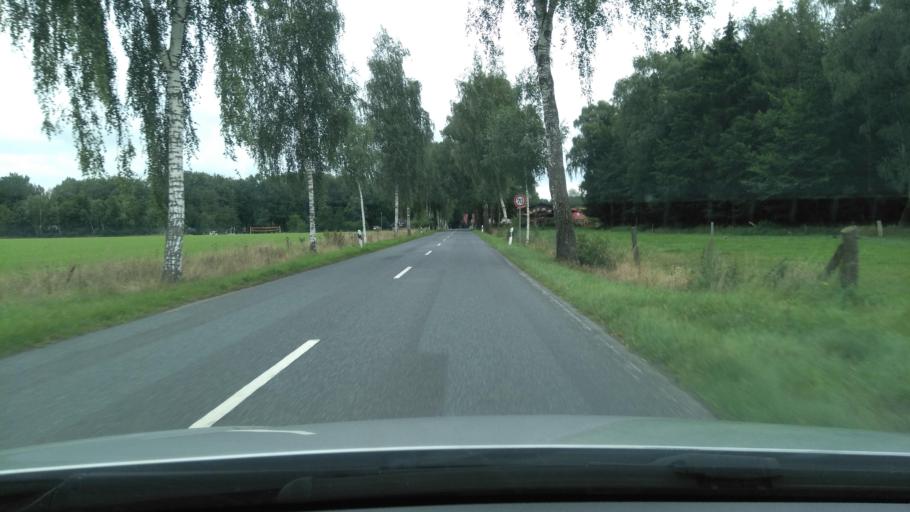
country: DE
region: Lower Saxony
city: Walsrode
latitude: 52.8958
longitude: 9.5826
